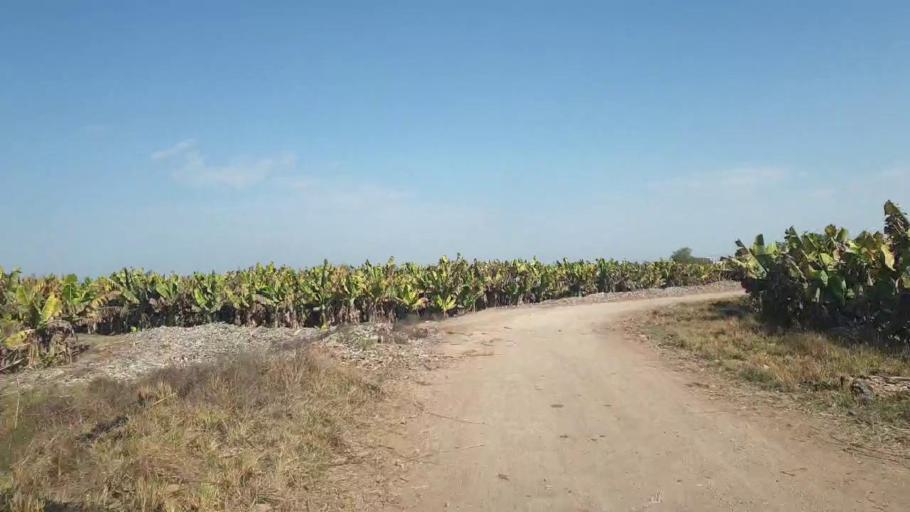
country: PK
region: Sindh
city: Sakrand
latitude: 25.9848
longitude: 68.3470
